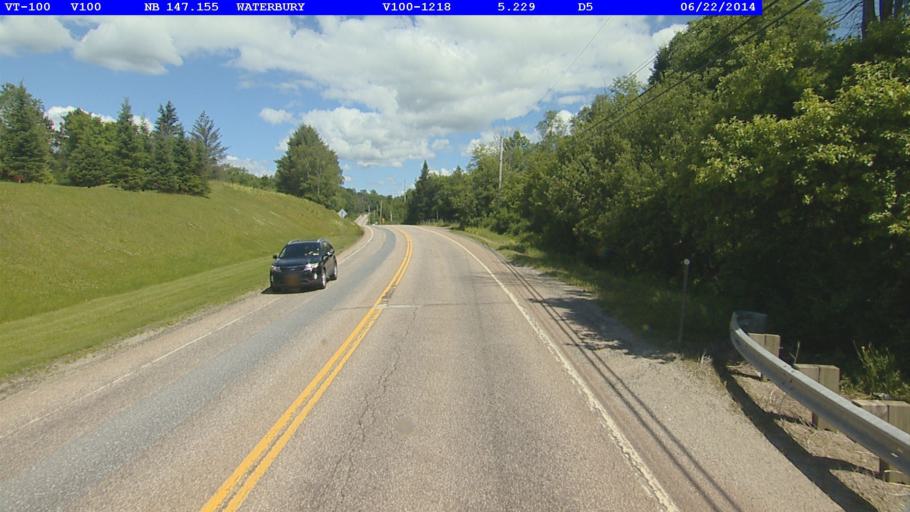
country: US
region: Vermont
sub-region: Washington County
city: Waterbury
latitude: 44.4044
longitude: -72.7189
